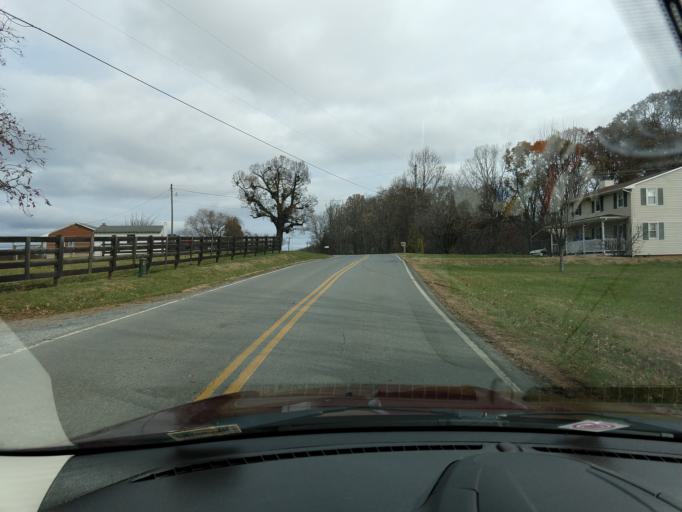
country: US
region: Virginia
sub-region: Franklin County
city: North Shore
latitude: 37.2419
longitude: -79.6734
